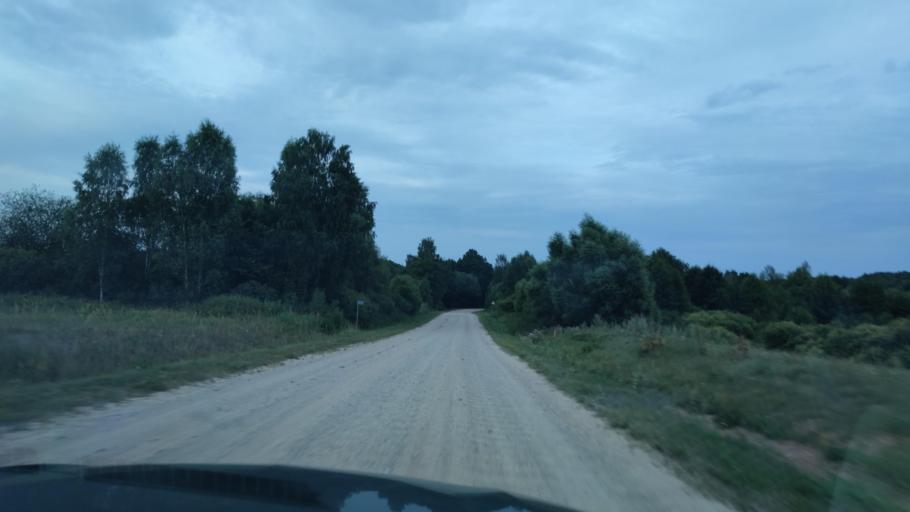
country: BY
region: Vitebsk
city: Mosar
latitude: 55.0736
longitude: 27.2052
